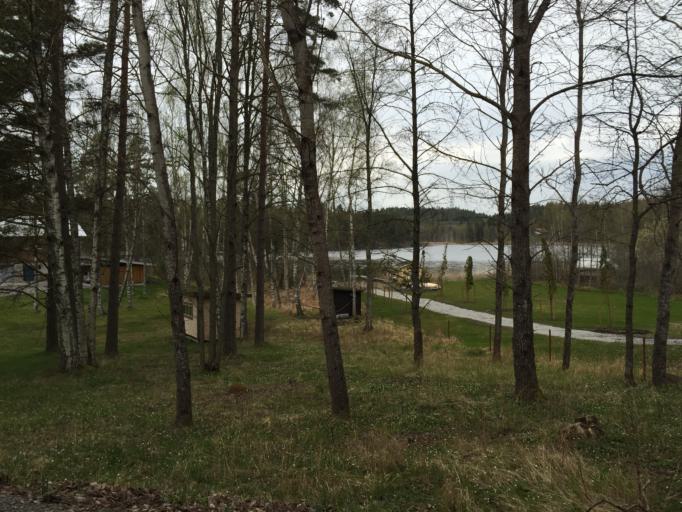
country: SE
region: Stockholm
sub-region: Salems Kommun
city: Ronninge
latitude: 59.1919
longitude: 17.7114
